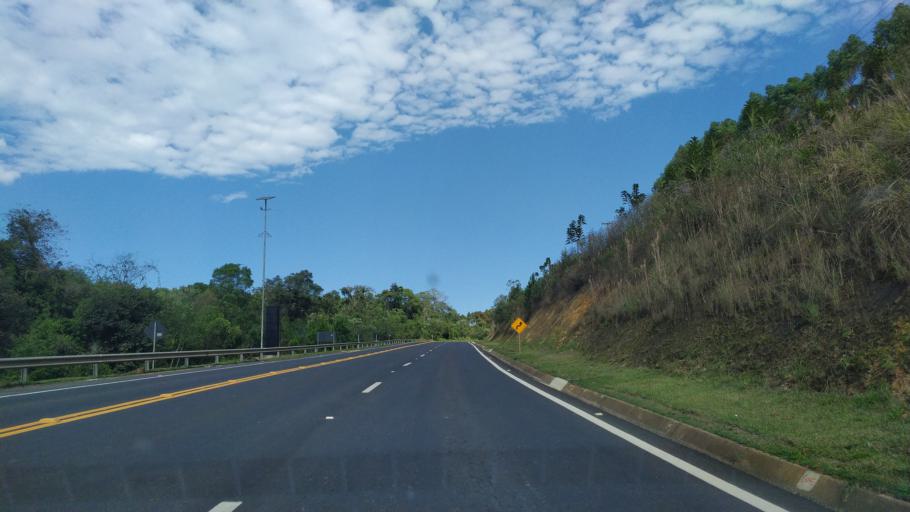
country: BR
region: Parana
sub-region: Telemaco Borba
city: Telemaco Borba
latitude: -24.2976
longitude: -50.7036
